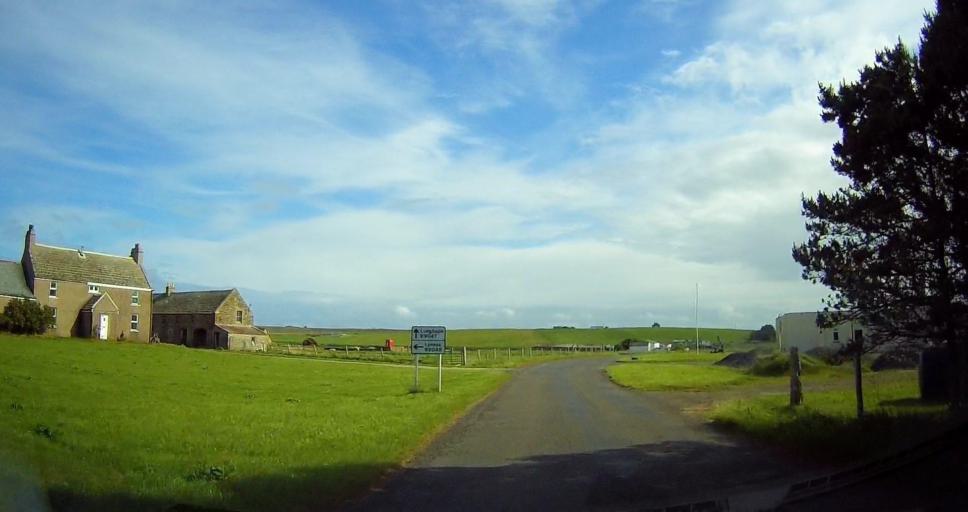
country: GB
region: Scotland
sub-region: Orkney Islands
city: Stromness
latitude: 58.8327
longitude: -3.2067
